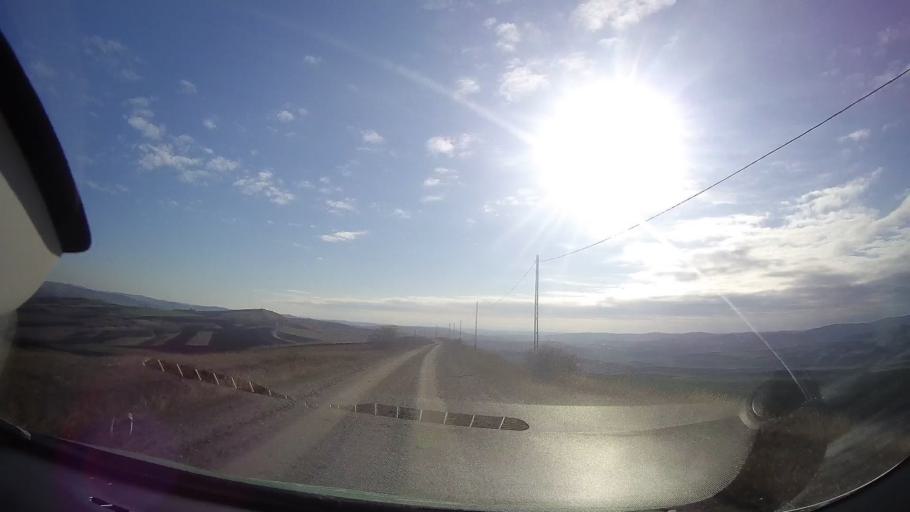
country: RO
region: Mures
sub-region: Comuna Saulia
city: Saulia
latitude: 46.5895
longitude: 24.2216
